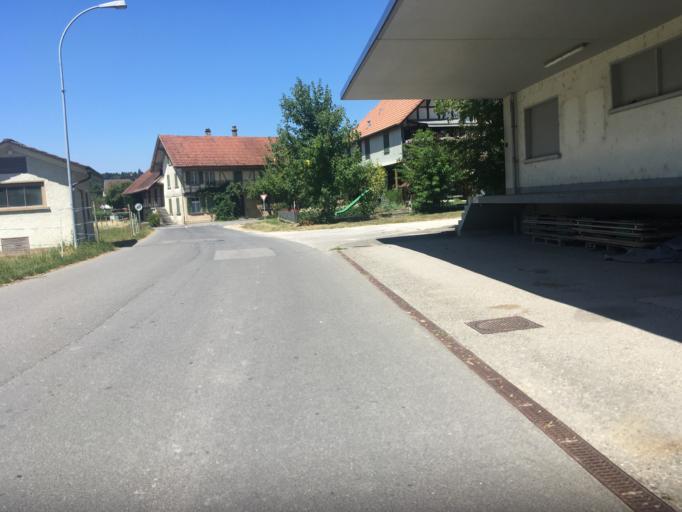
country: CH
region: Bern
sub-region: Seeland District
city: Grossaffoltern
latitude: 47.0833
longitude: 7.4013
